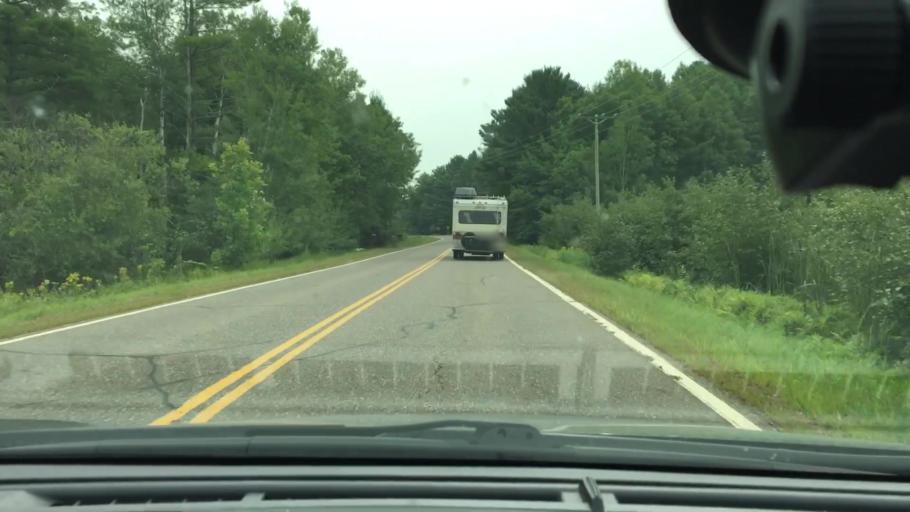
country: US
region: Minnesota
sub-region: Aitkin County
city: Aitkin
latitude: 46.4024
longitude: -93.7750
